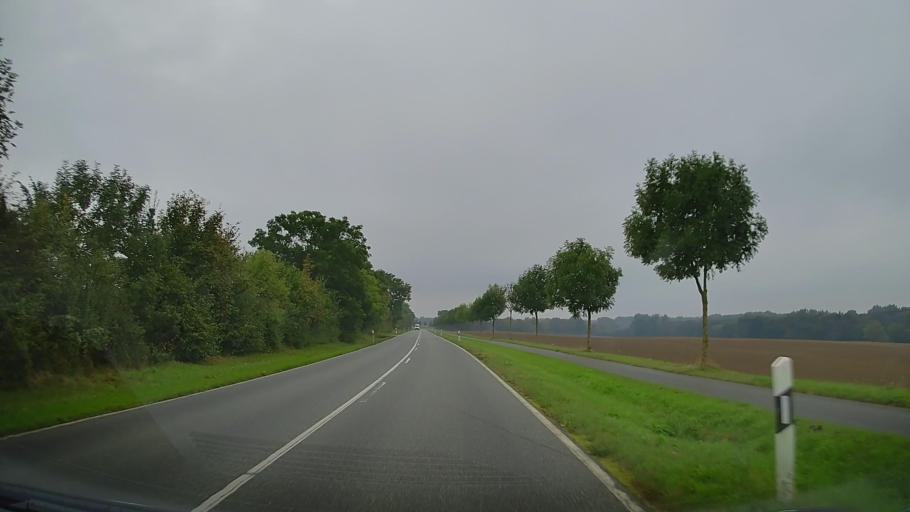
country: DE
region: Mecklenburg-Vorpommern
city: Ostseebad Boltenhagen
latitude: 53.9645
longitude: 11.2288
